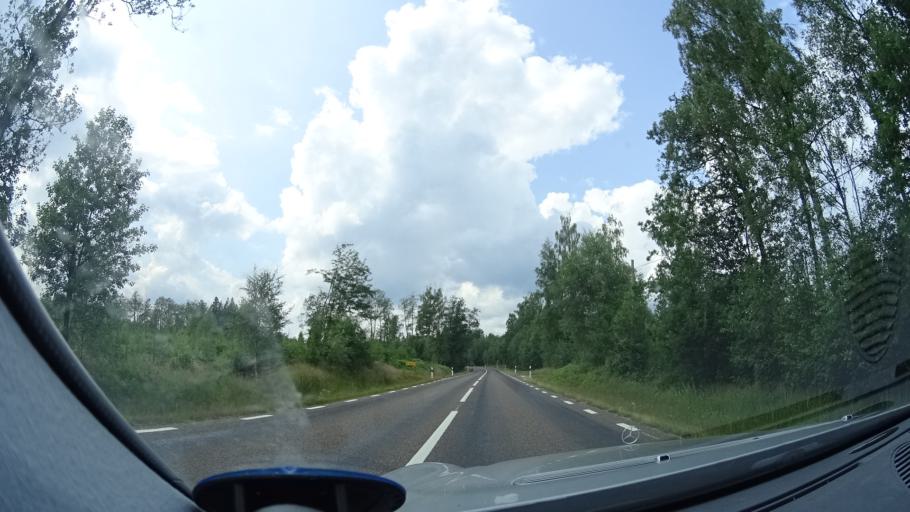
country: SE
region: Kalmar
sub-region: Emmaboda Kommun
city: Emmaboda
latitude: 56.6291
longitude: 15.6309
